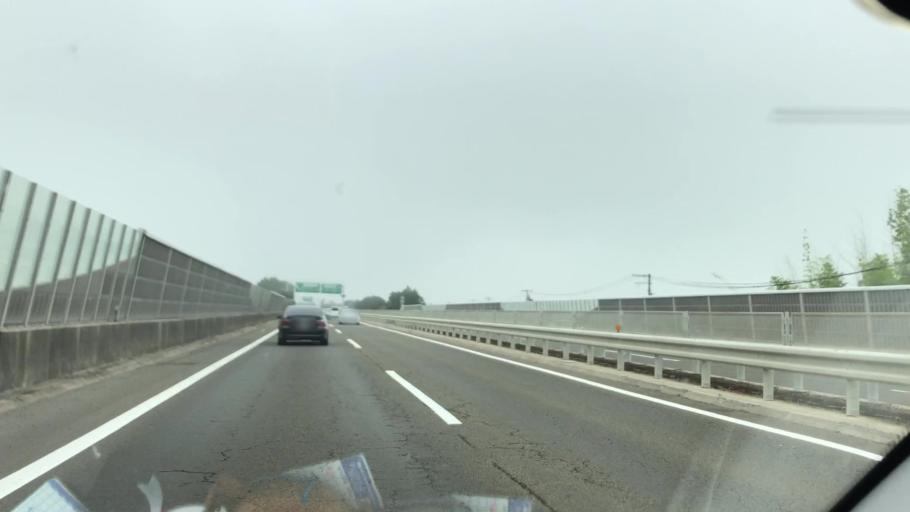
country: JP
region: Miyagi
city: Sendai
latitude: 38.2140
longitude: 140.9474
